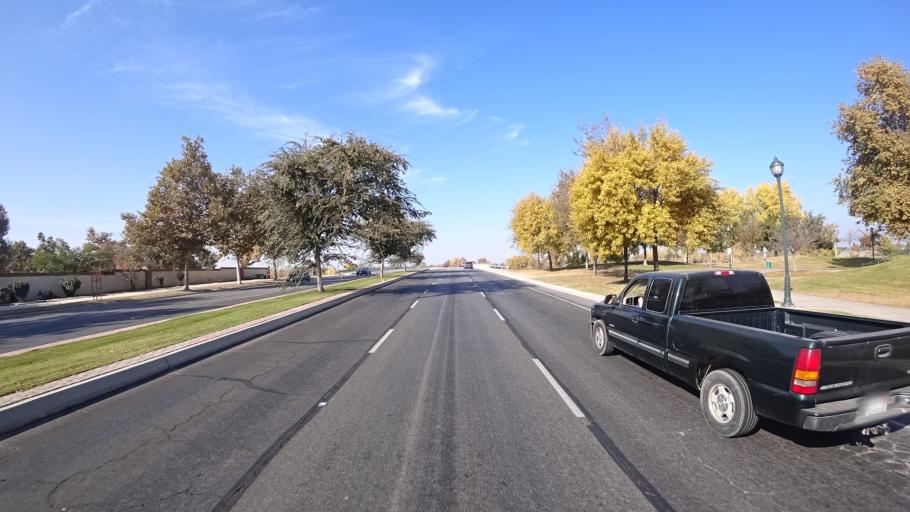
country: US
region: California
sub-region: Kern County
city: Rosedale
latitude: 35.3505
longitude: -119.1305
